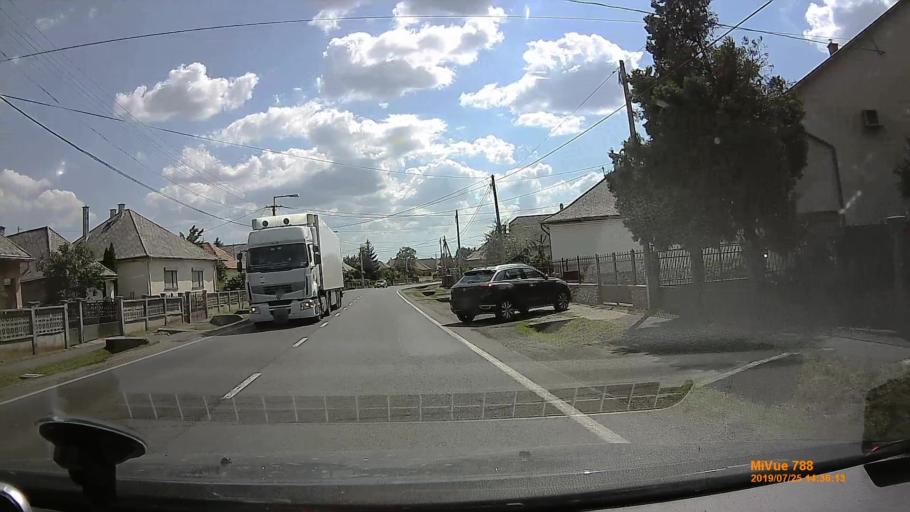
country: HU
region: Borsod-Abauj-Zemplen
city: Encs
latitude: 48.3224
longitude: 21.0874
